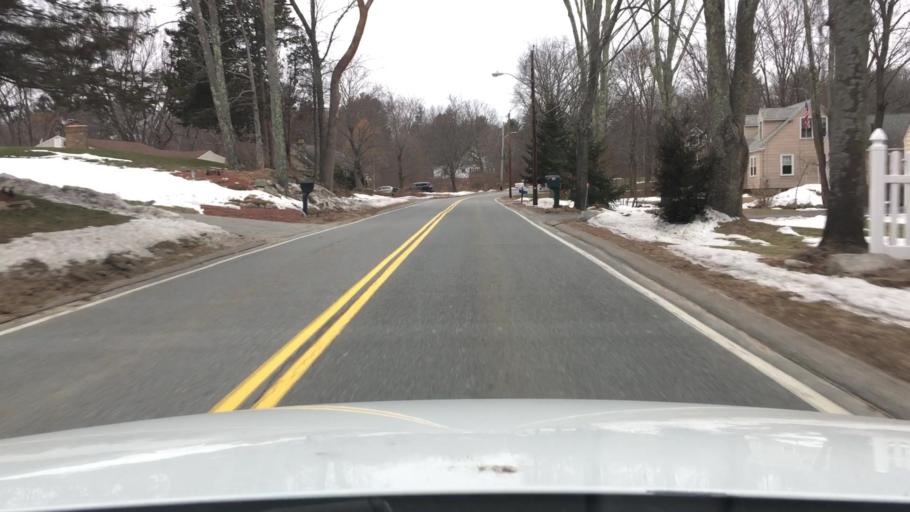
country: US
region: New Hampshire
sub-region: Rockingham County
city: Salem
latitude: 42.7967
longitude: -71.2273
